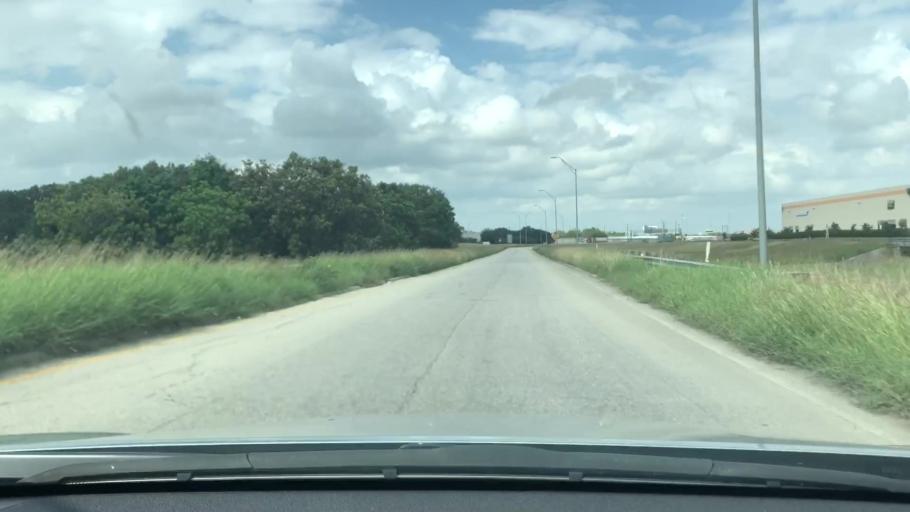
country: US
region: Texas
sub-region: Bexar County
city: Kirby
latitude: 29.4372
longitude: -98.3882
